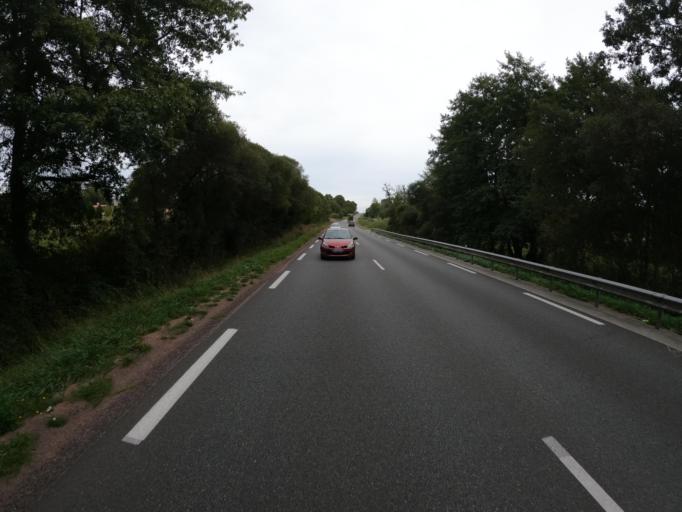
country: FR
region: Limousin
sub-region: Departement de la Haute-Vienne
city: Arnac-la-Poste
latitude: 46.2016
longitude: 1.3282
